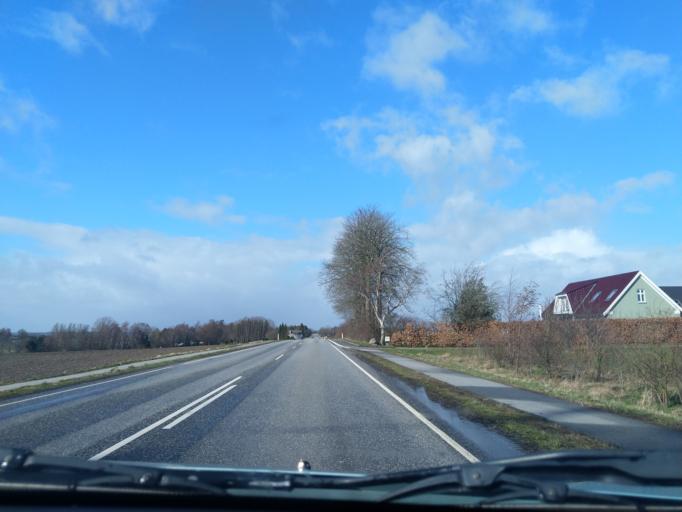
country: DK
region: Zealand
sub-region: Naestved Kommune
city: Naestved
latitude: 55.2792
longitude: 11.7207
